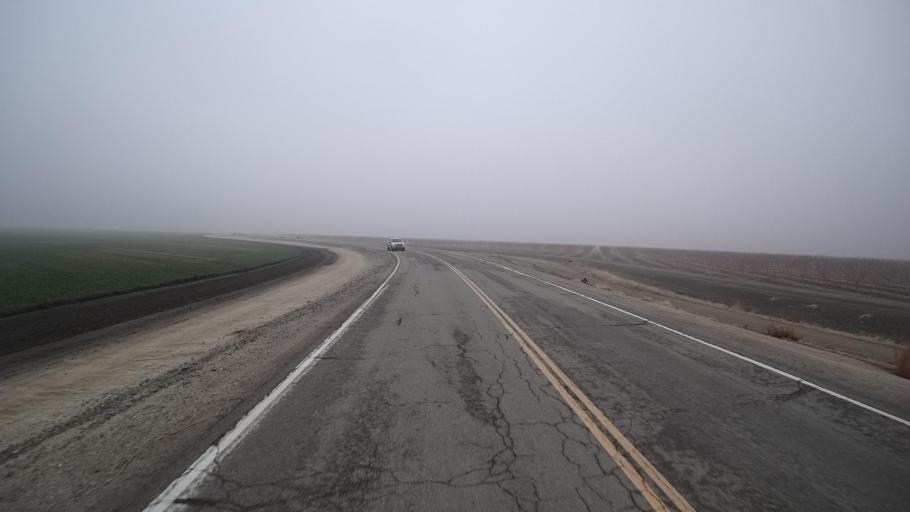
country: US
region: California
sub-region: Kern County
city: Buttonwillow
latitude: 35.4345
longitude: -119.5429
